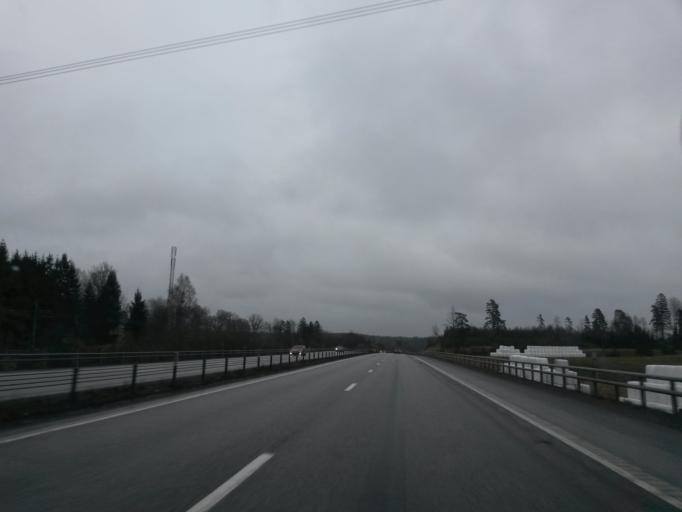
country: SE
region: Vaestra Goetaland
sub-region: Uddevalla Kommun
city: Uddevalla
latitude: 58.3326
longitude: 12.1008
